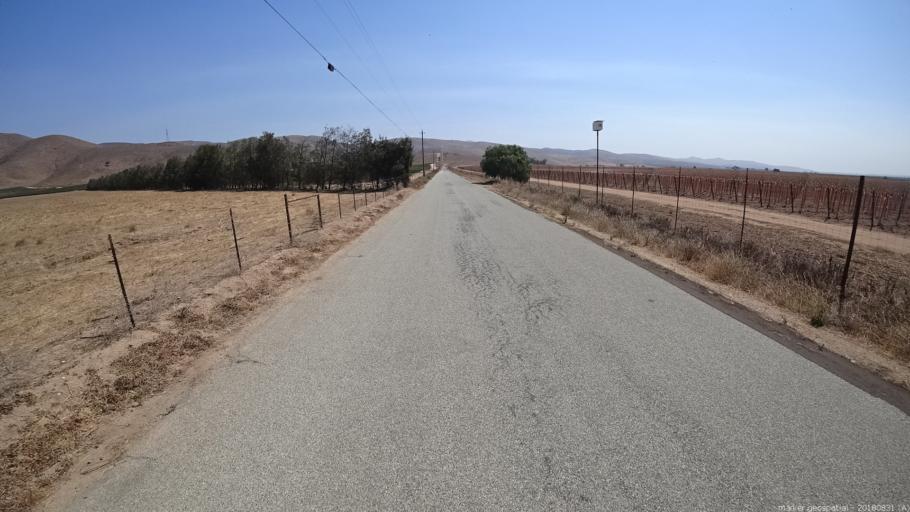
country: US
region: California
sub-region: Monterey County
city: Soledad
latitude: 36.4451
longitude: -121.3104
